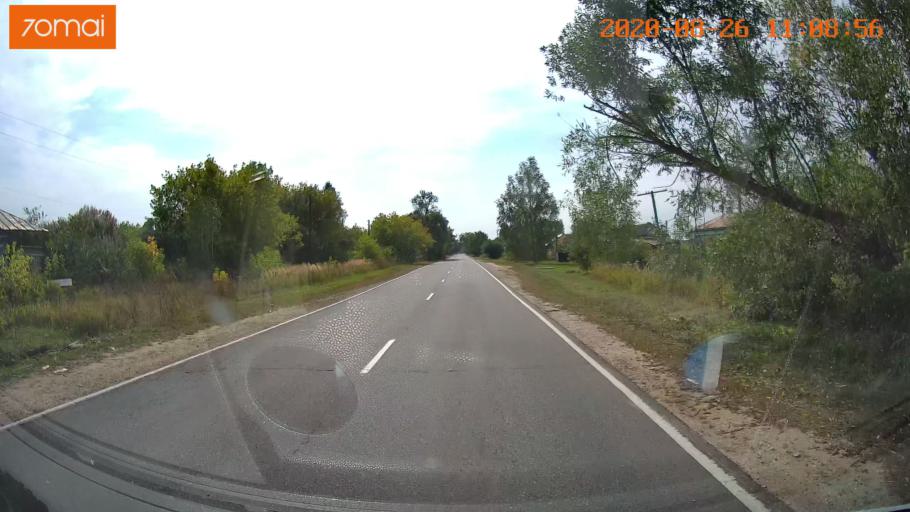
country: RU
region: Rjazan
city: Izhevskoye
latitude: 54.4973
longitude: 41.1229
